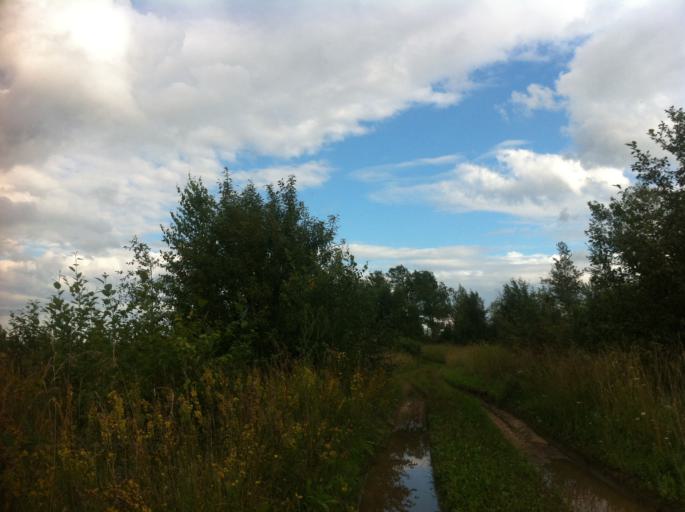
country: RU
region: Pskov
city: Izborsk
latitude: 57.8194
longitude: 27.9713
